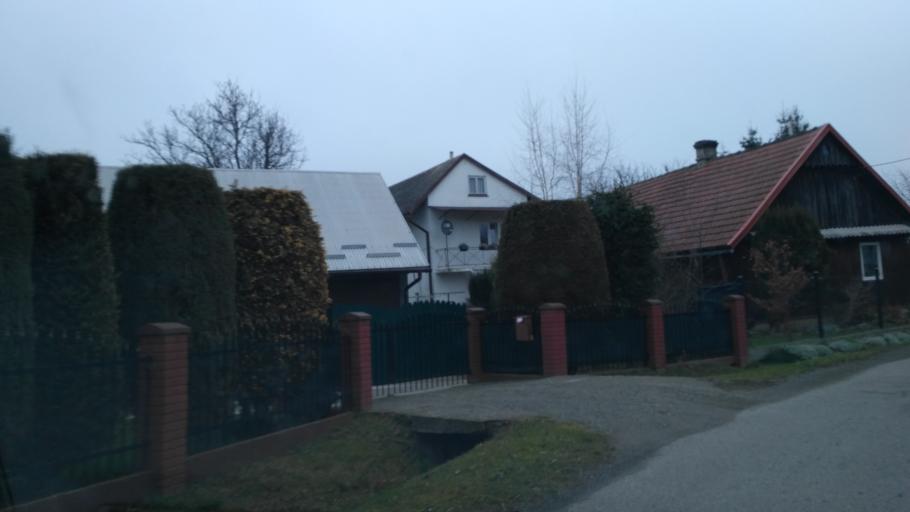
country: PL
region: Subcarpathian Voivodeship
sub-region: Powiat jaroslawski
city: Pawlosiow
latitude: 49.9680
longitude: 22.6459
